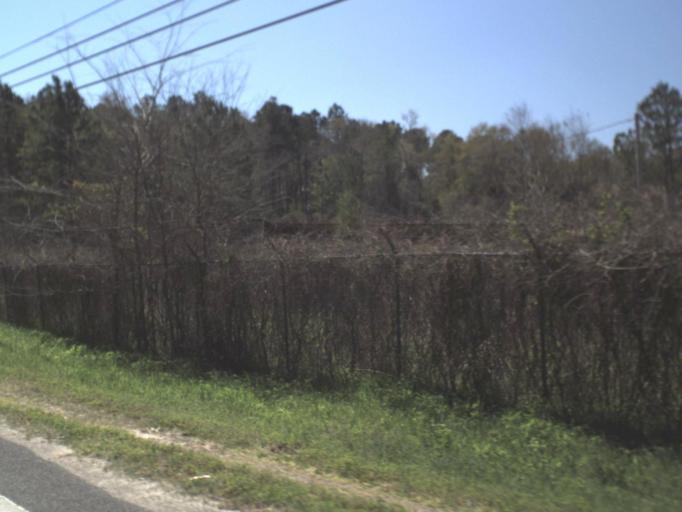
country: US
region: Florida
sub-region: Leon County
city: Woodville
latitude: 30.2823
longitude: -84.2407
